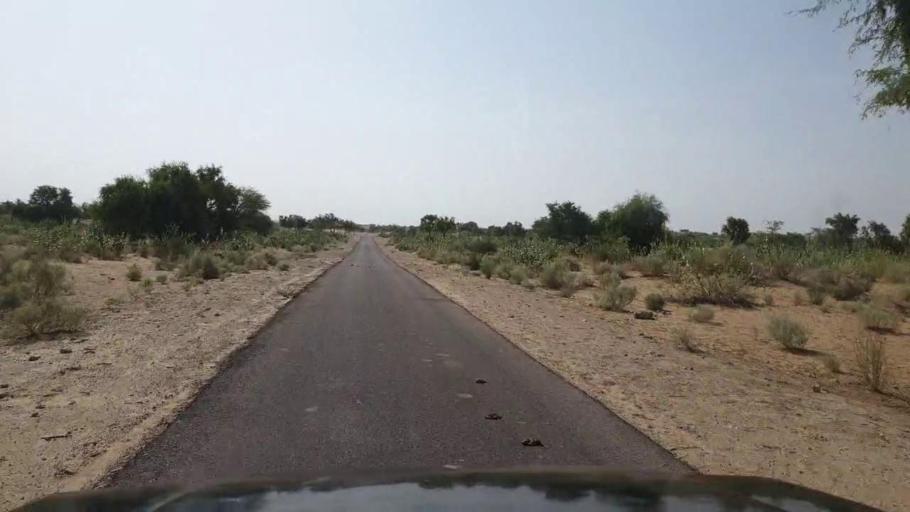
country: PK
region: Sindh
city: Islamkot
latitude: 24.9415
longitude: 70.0753
